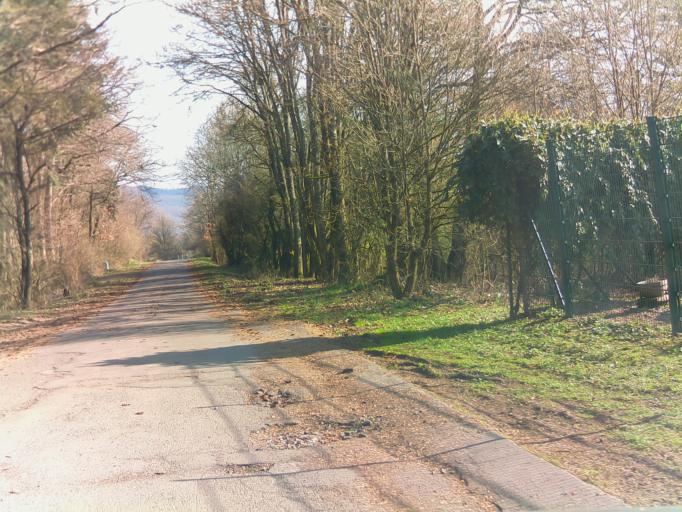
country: DE
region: Rheinland-Pfalz
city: Idar-Oberstein
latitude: 49.6880
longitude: 7.3241
